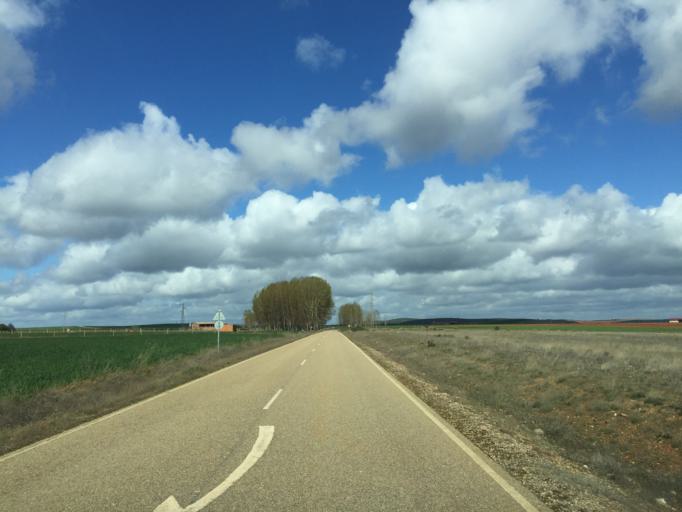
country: ES
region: Castille and Leon
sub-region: Provincia de Zamora
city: Palacios del Pan
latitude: 41.5786
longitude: -5.9265
